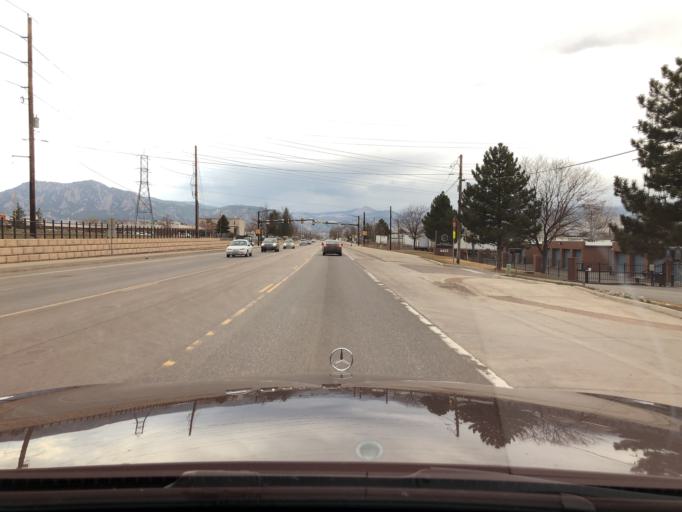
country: US
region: Colorado
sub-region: Boulder County
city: Gunbarrel
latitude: 40.0147
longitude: -105.1987
